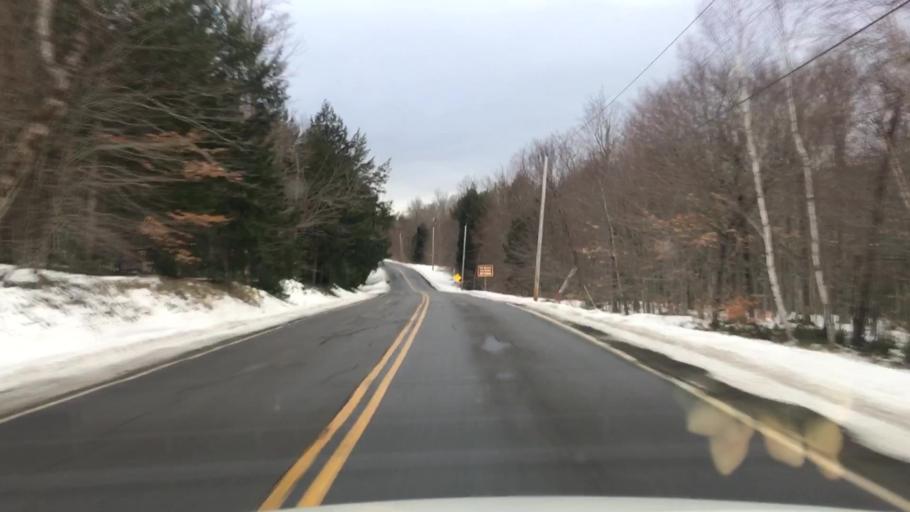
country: US
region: Maine
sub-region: Hancock County
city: Franklin
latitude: 44.6247
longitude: -68.0861
